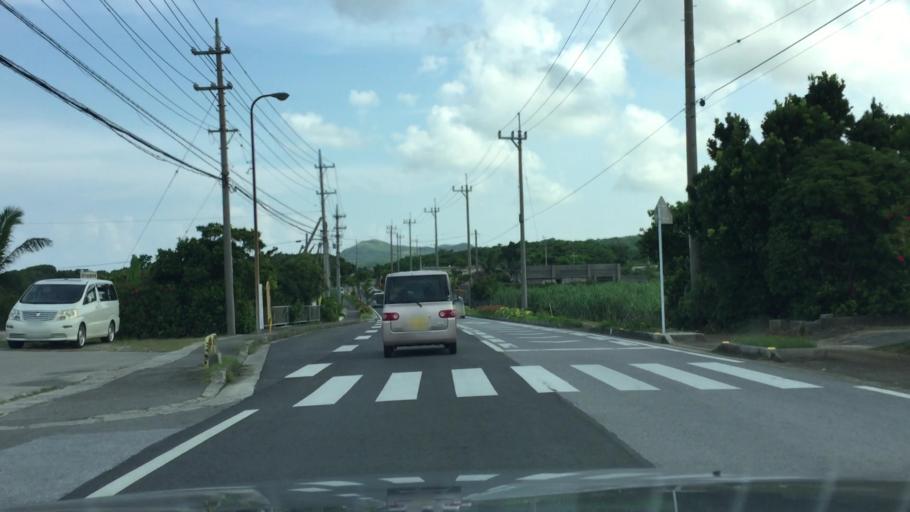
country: JP
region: Okinawa
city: Ishigaki
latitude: 24.4385
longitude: 124.2491
